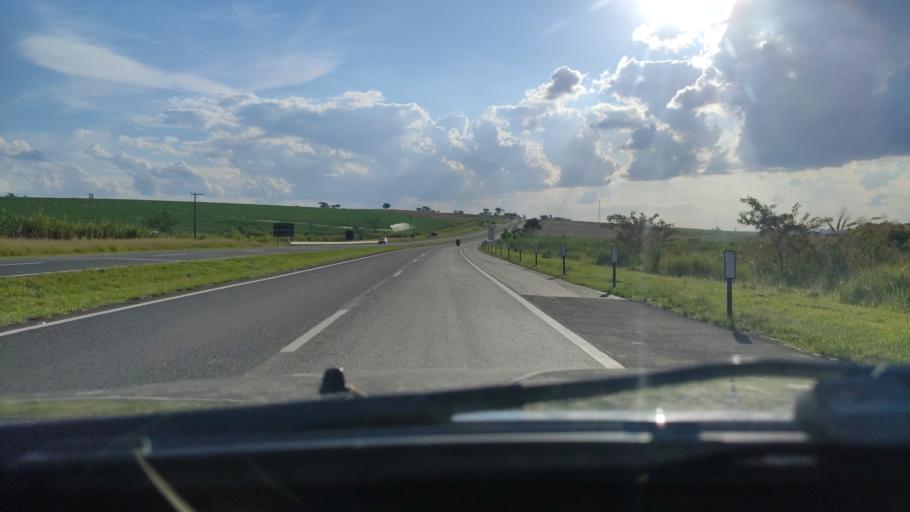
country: BR
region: Sao Paulo
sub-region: Mogi-Mirim
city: Mogi Mirim
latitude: -22.4567
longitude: -46.9045
